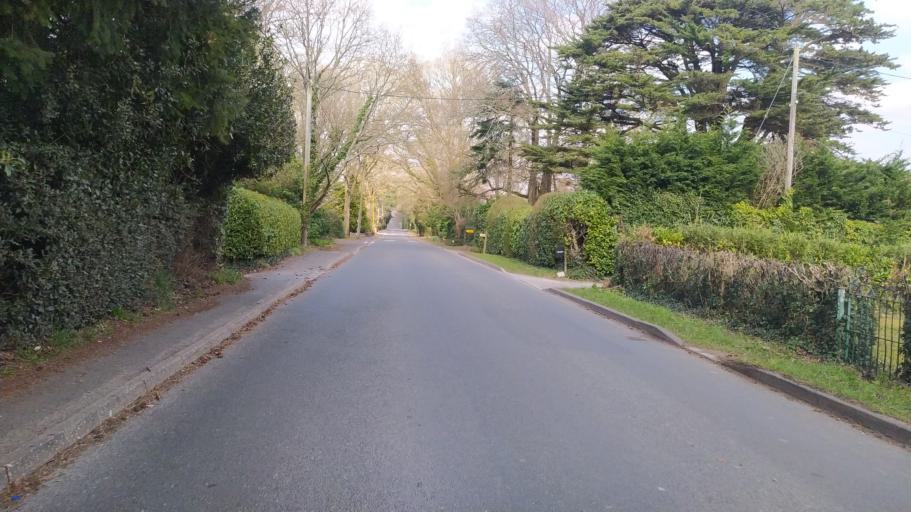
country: GB
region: England
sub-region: Hampshire
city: West Wellow
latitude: 50.9667
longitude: -1.5638
